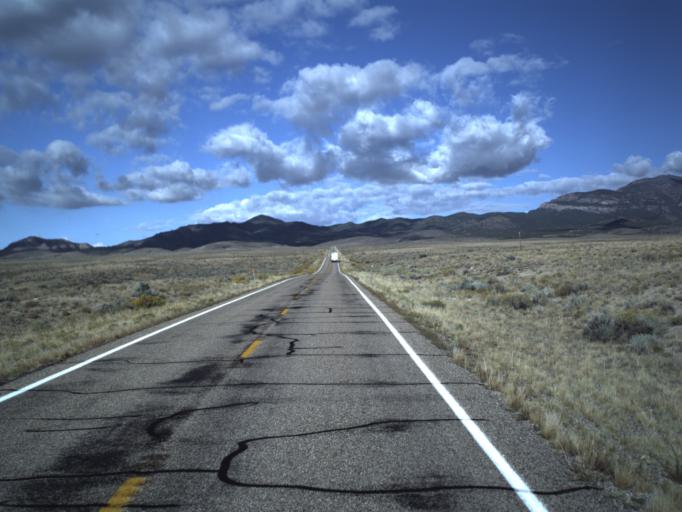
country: US
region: Utah
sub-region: Beaver County
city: Milford
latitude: 38.4439
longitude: -113.1761
